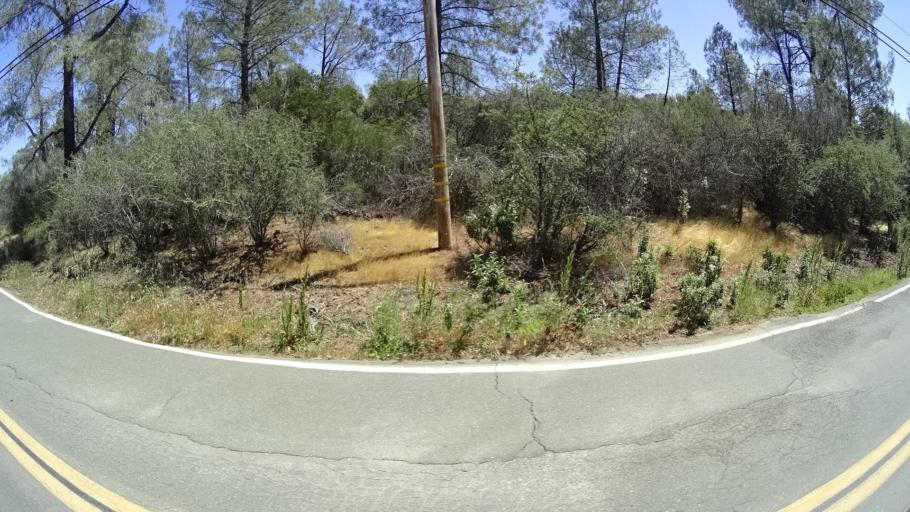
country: US
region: California
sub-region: Lake County
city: Hidden Valley Lake
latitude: 38.8257
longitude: -122.5441
